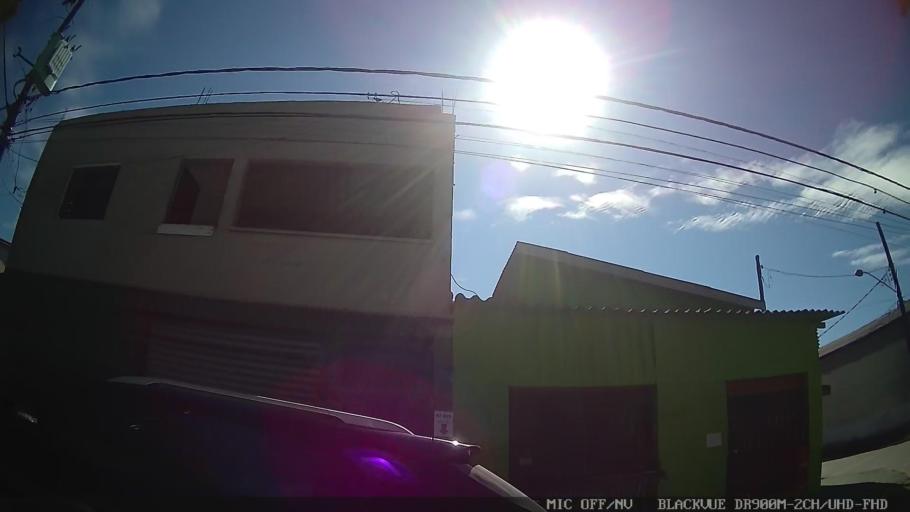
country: BR
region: Sao Paulo
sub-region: Santos
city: Santos
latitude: -23.9489
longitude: -46.2914
